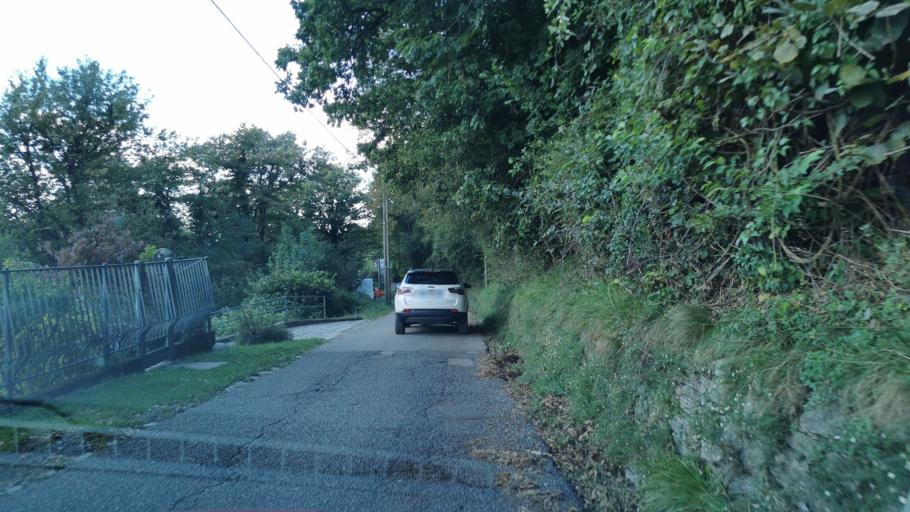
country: IT
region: Lombardy
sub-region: Provincia di Como
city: Moltrasio
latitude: 45.8586
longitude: 9.0875
